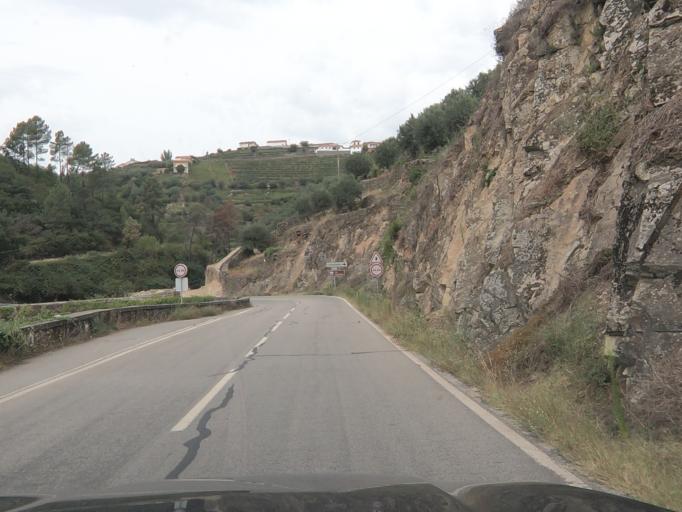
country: PT
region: Vila Real
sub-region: Santa Marta de Penaguiao
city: Santa Marta de Penaguiao
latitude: 41.2258
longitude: -7.7701
